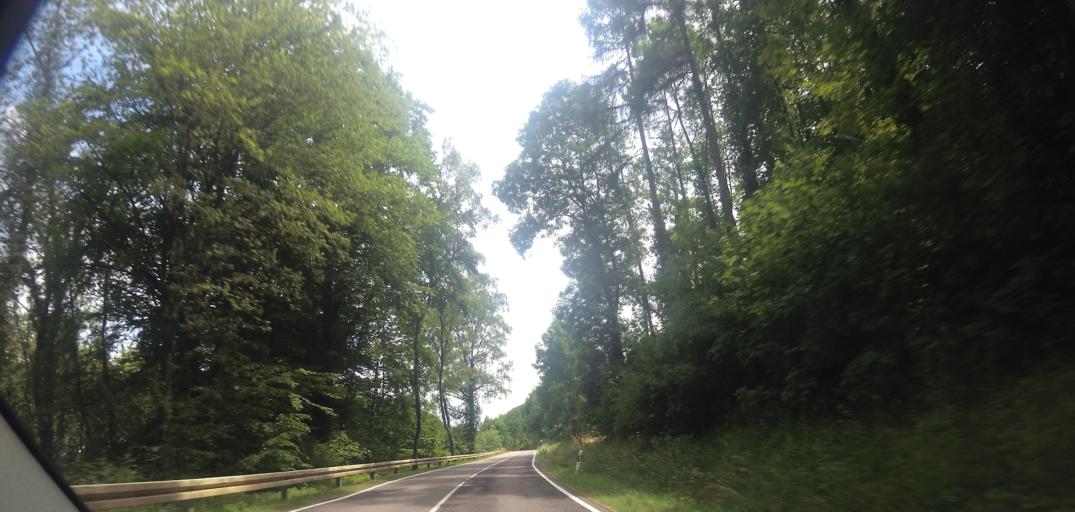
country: DE
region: Saarland
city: Merzig
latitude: 49.4230
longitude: 6.5687
